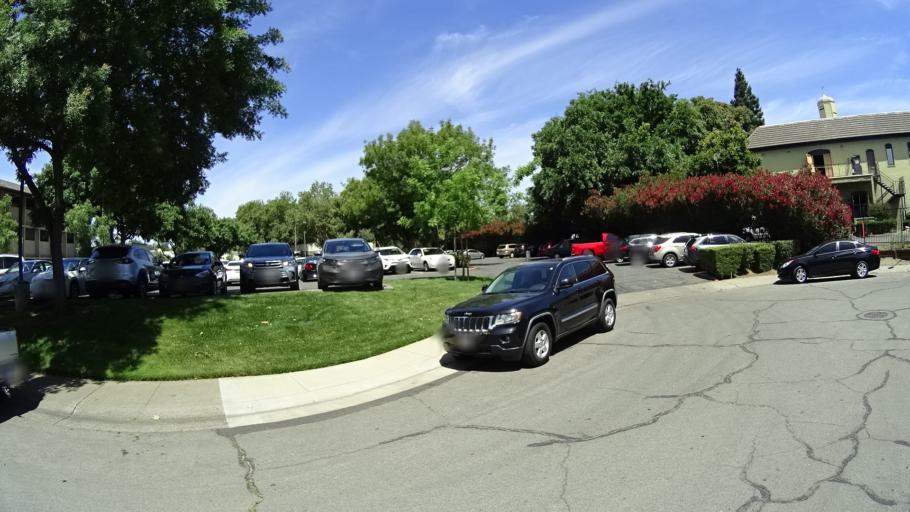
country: US
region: California
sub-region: Sacramento County
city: Arden-Arcade
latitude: 38.5733
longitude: -121.4113
